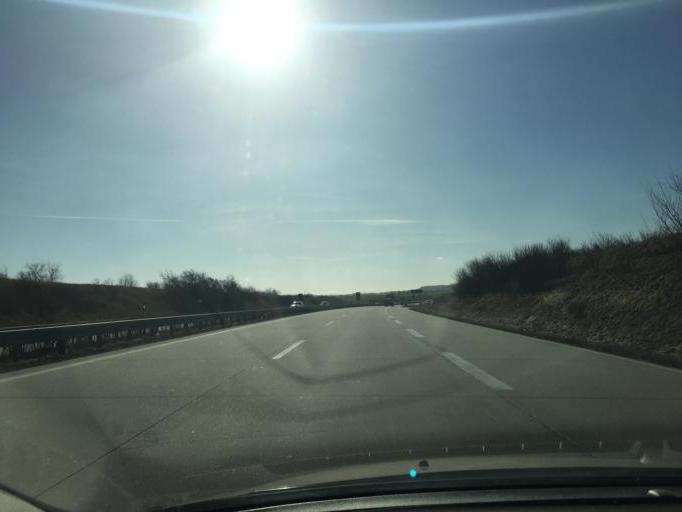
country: DE
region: Saxony
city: Niederfrohna
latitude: 50.9055
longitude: 12.7322
